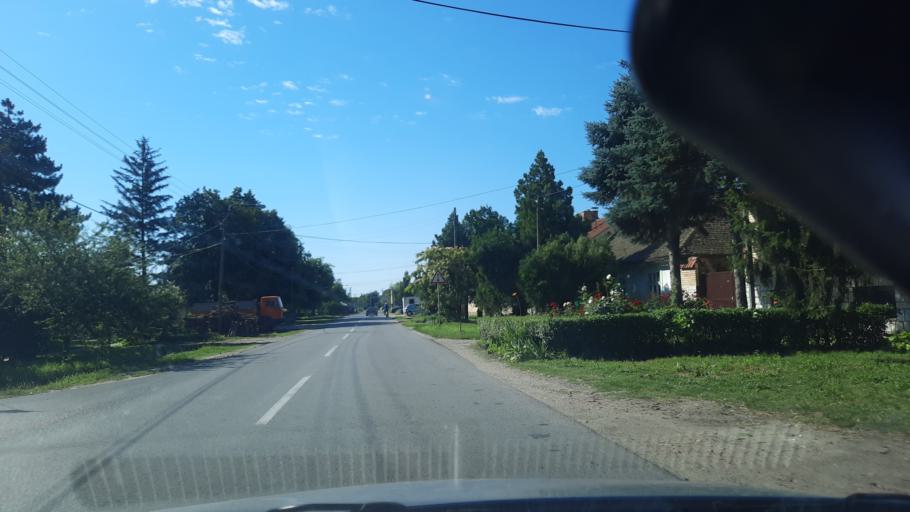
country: RS
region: Autonomna Pokrajina Vojvodina
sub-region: Juznobanatski Okrug
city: Kovin
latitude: 44.7506
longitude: 20.9703
